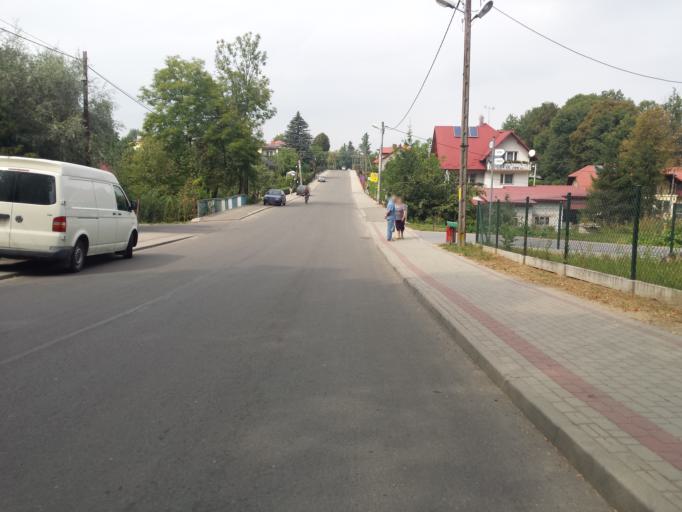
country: PL
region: Subcarpathian Voivodeship
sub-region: Powiat rzeszowski
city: Dynow
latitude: 49.8157
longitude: 22.2302
